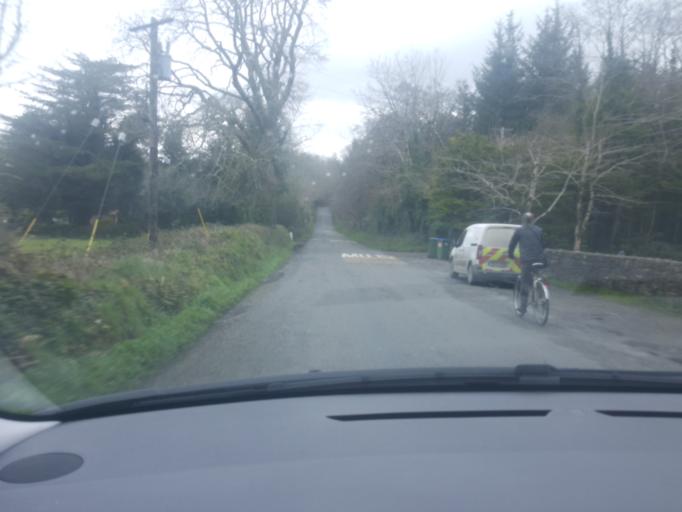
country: IE
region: Munster
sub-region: Ciarrai
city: Cill Airne
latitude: 52.0751
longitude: -9.5084
